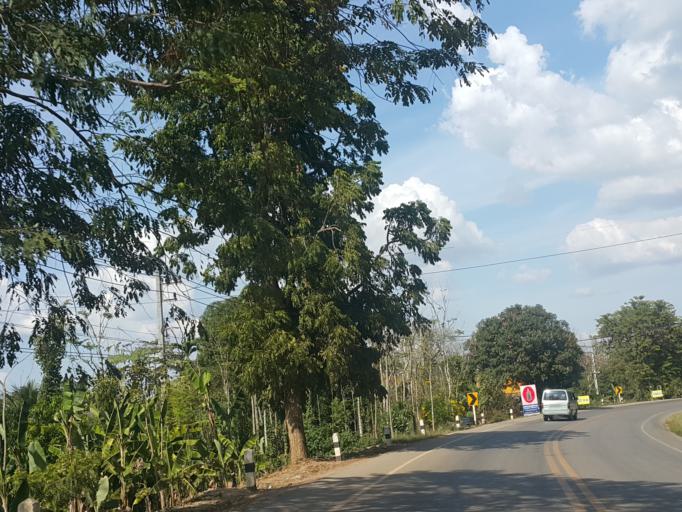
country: TH
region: Sukhothai
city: Sawankhalok
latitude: 17.2760
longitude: 99.8296
